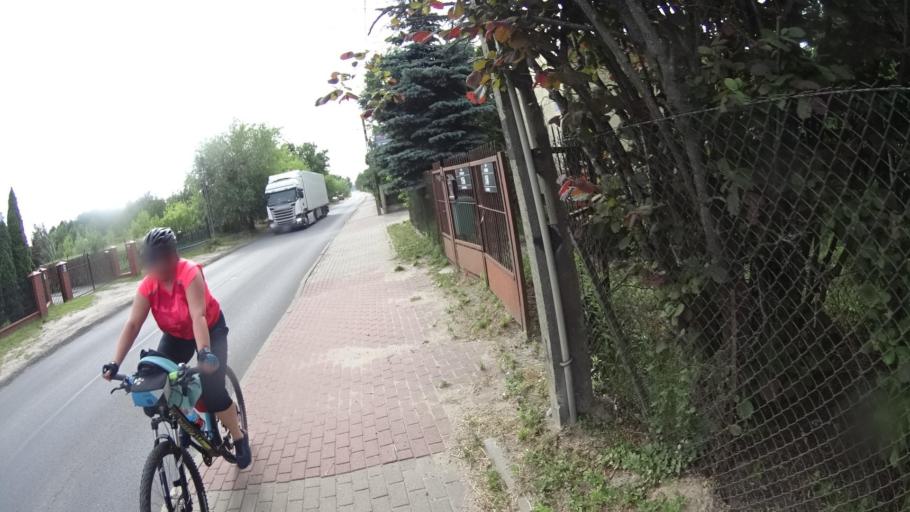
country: PL
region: Masovian Voivodeship
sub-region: Powiat warszawski zachodni
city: Ozarow Mazowiecki
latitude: 52.1910
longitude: 20.7489
